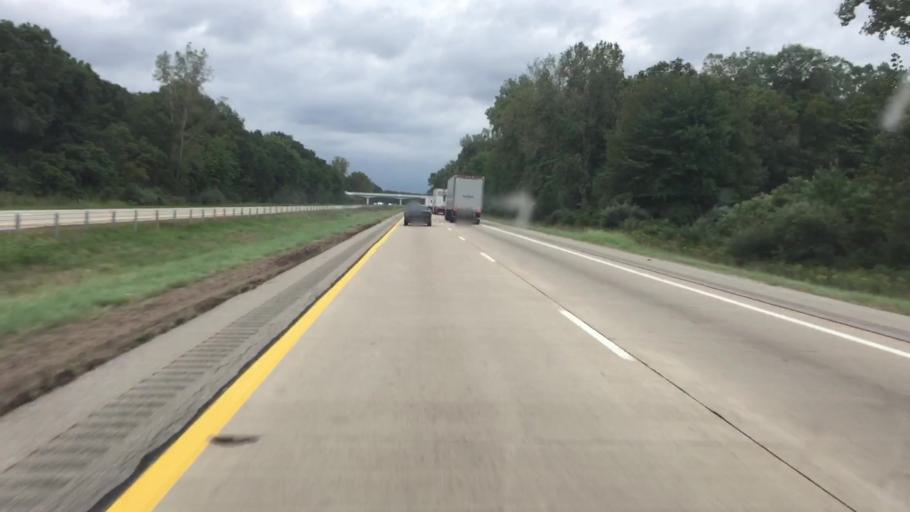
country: US
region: Michigan
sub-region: Monroe County
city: Petersburg
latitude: 41.8706
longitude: -83.6613
